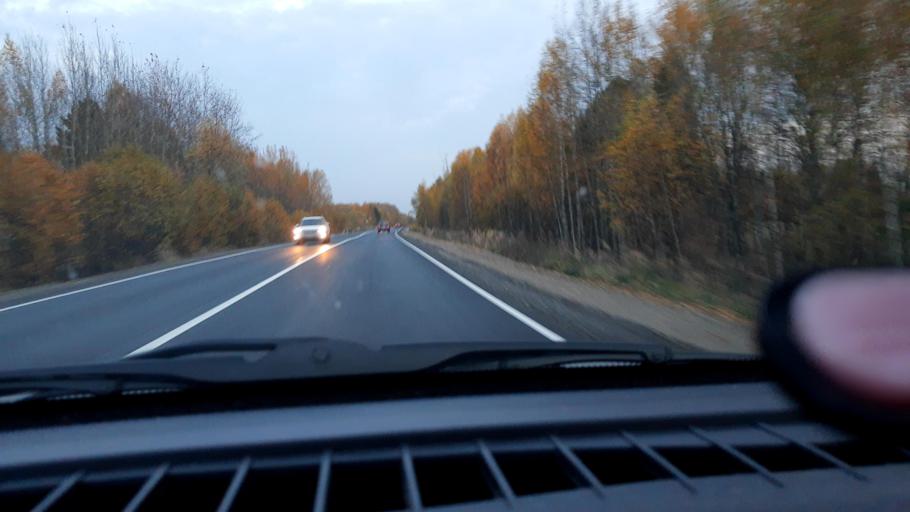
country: RU
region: Nizjnij Novgorod
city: Novaya Balakhna
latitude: 56.5752
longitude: 43.7010
